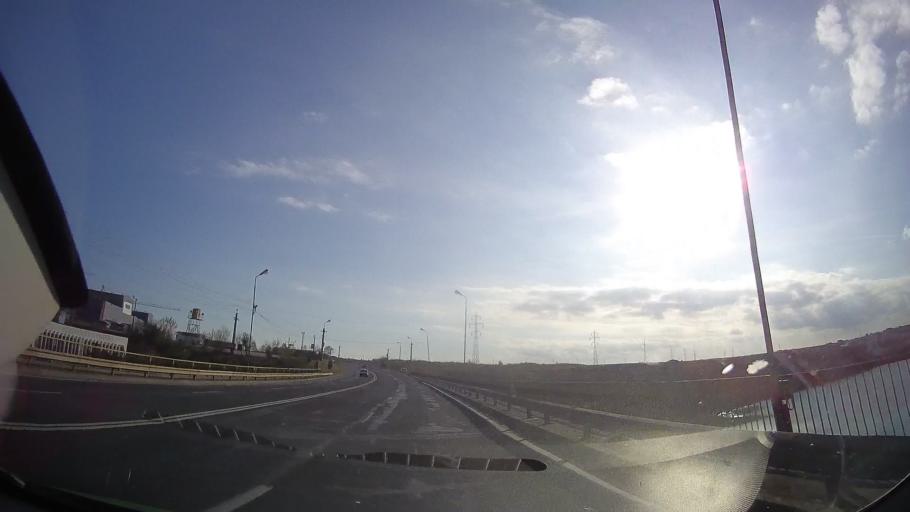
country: RO
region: Constanta
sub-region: Municipiul Mangalia
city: Mangalia
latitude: 43.8004
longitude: 28.5592
